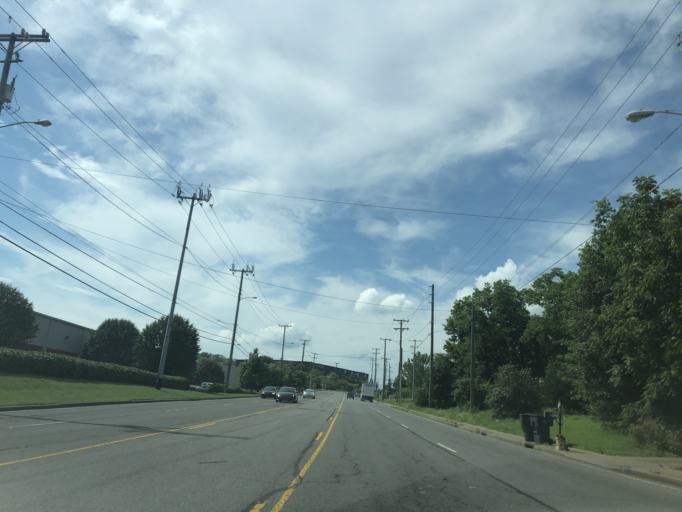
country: US
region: Tennessee
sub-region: Davidson County
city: Nashville
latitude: 36.2154
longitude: -86.7799
